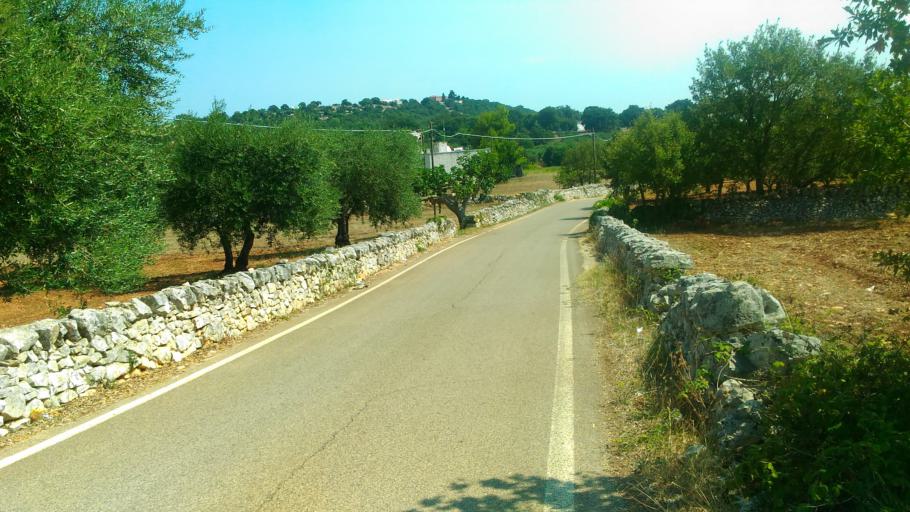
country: IT
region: Apulia
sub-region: Provincia di Bari
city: Locorotondo
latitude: 40.7503
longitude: 17.3651
